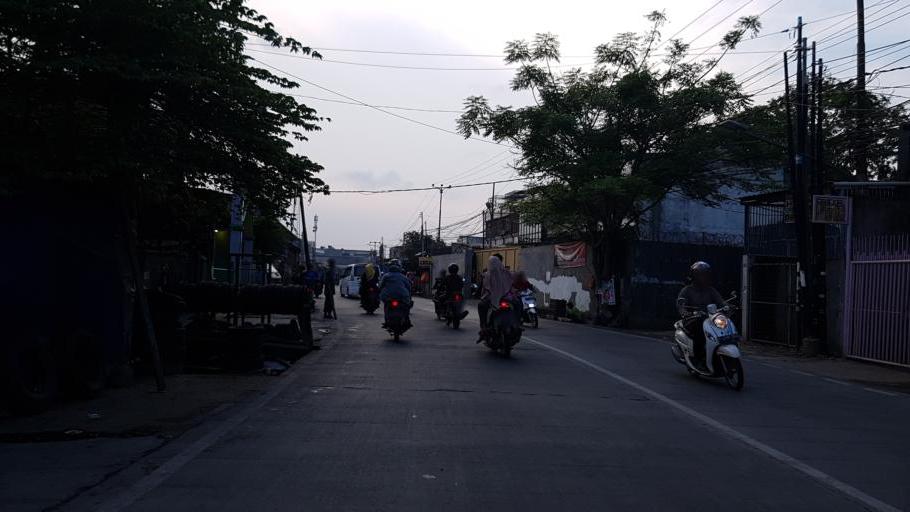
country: ID
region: Jakarta Raya
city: Jakarta
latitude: -6.1414
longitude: 106.7747
